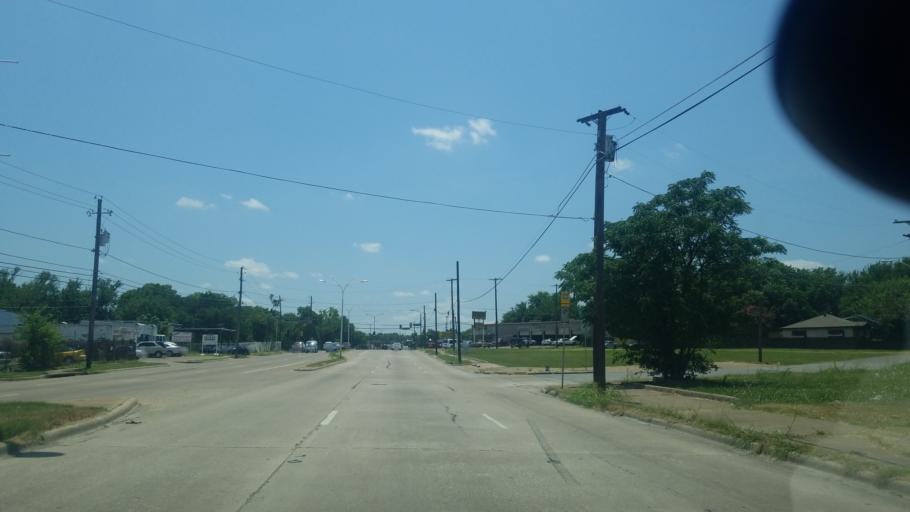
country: US
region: Texas
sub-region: Dallas County
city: Dallas
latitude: 32.7439
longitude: -96.7876
